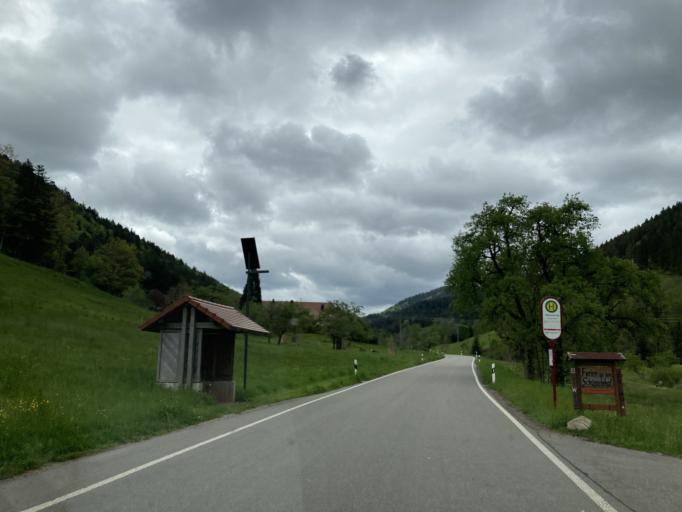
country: DE
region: Baden-Wuerttemberg
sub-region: Freiburg Region
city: Schonach im Schwarzwald
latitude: 48.1961
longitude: 8.1609
